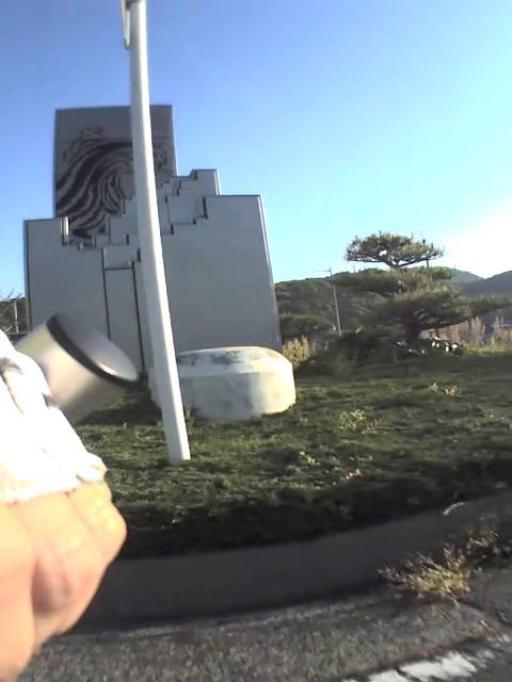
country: JP
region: Yamaguchi
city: Nagato
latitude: 34.3955
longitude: 131.2001
